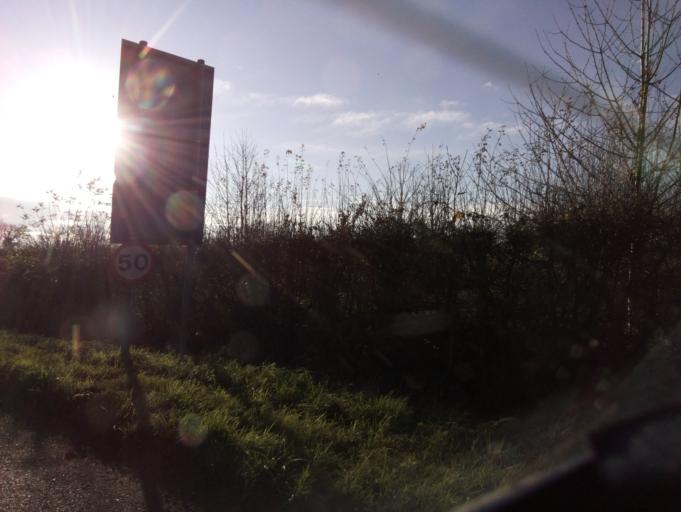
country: GB
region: England
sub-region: Derbyshire
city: Etwall
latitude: 52.8610
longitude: -1.6017
